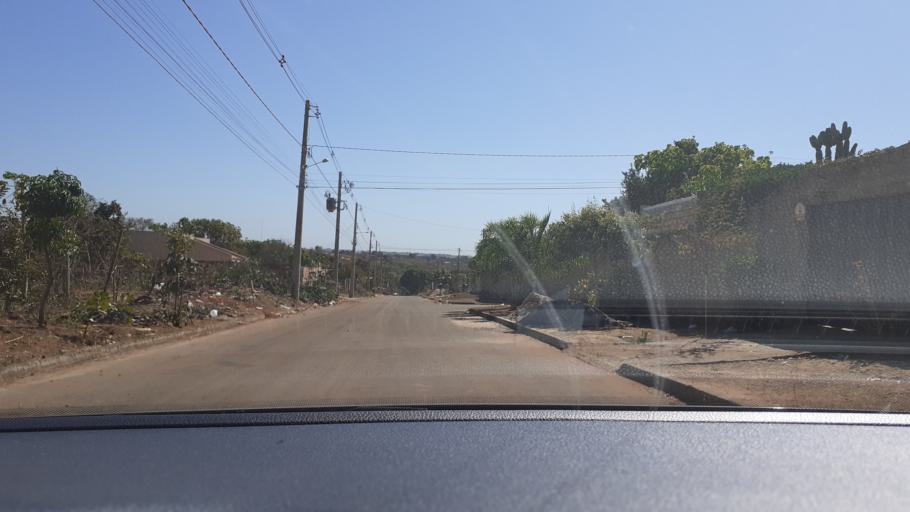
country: BR
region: Goias
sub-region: Aparecida De Goiania
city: Aparecida de Goiania
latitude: -16.8804
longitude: -49.2574
